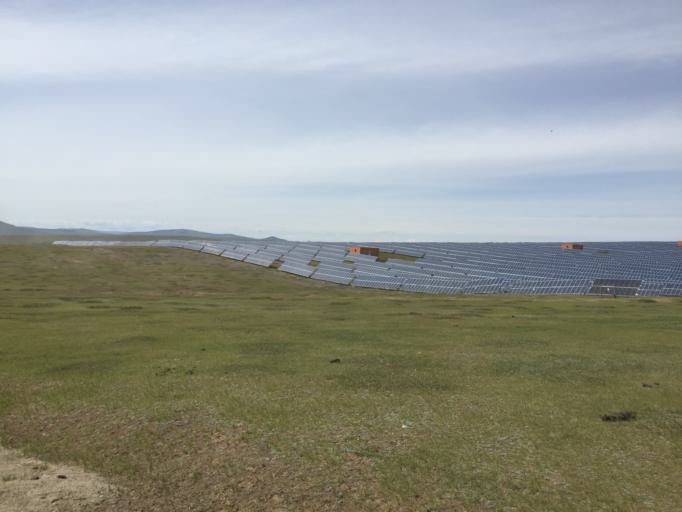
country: MN
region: Darhan Uul
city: Darhan
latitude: 49.3971
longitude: 105.9448
